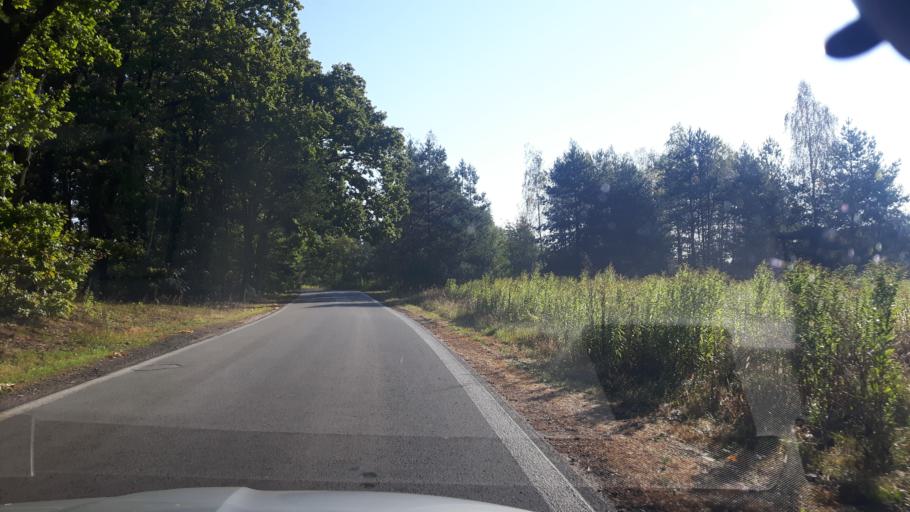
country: PL
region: Masovian Voivodeship
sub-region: Warszawa
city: Bialoleka
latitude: 52.3494
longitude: 21.0099
